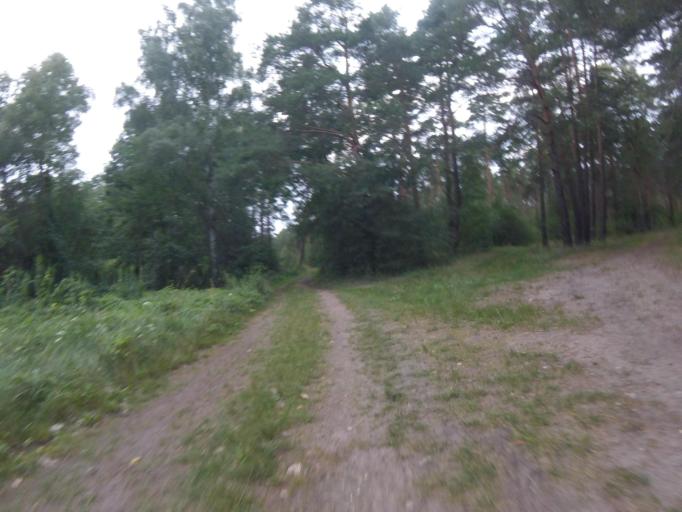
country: DE
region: Brandenburg
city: Gross Koris
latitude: 52.1572
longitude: 13.6812
